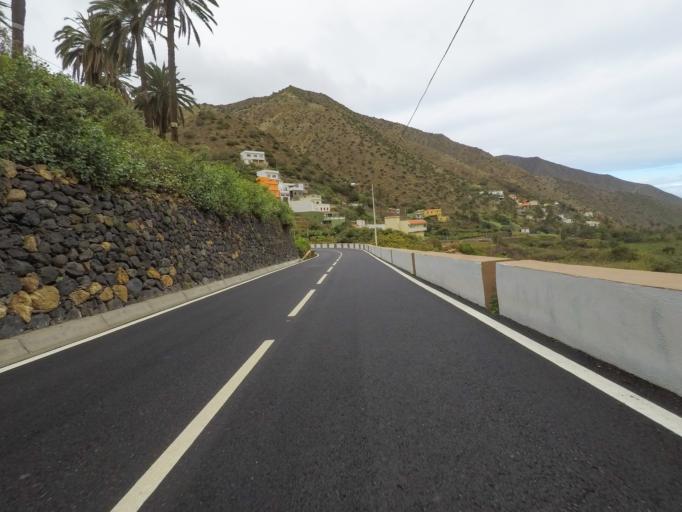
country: ES
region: Canary Islands
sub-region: Provincia de Santa Cruz de Tenerife
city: Vallehermosa
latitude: 28.1835
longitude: -17.2643
